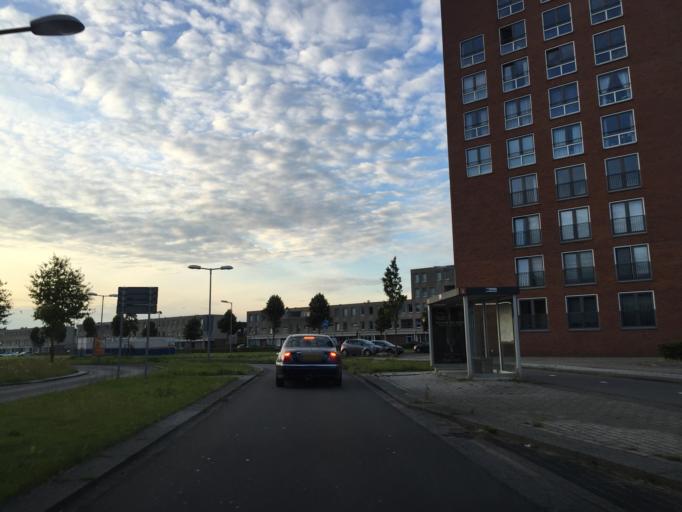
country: NL
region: South Holland
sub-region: Gemeente Rijnwoude
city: Benthuizen
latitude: 52.0654
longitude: 4.5342
